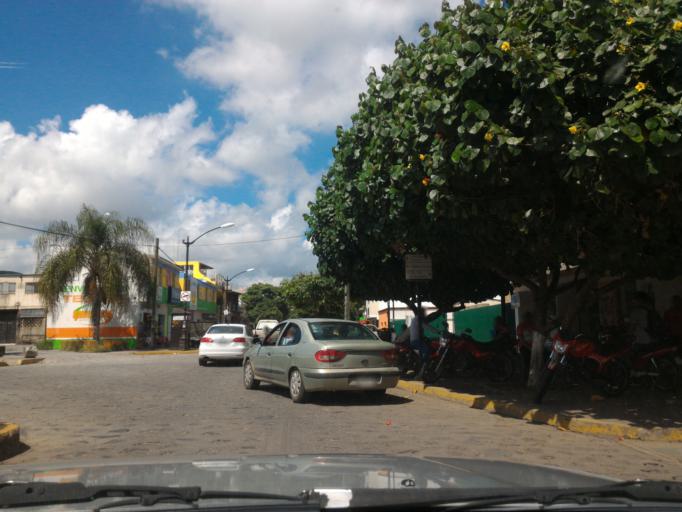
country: MX
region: Jalisco
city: Tequila
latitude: 20.8822
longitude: -103.8331
